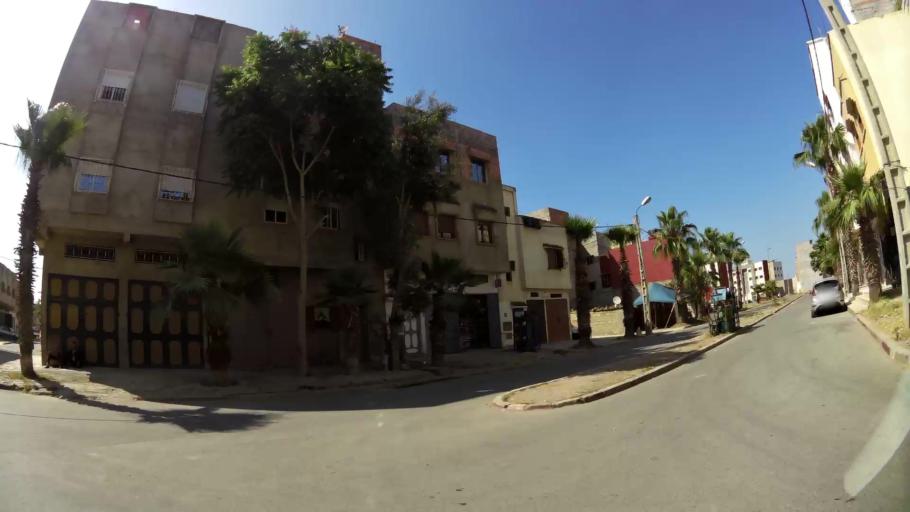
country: MA
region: Rabat-Sale-Zemmour-Zaer
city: Sale
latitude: 34.0698
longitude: -6.7726
